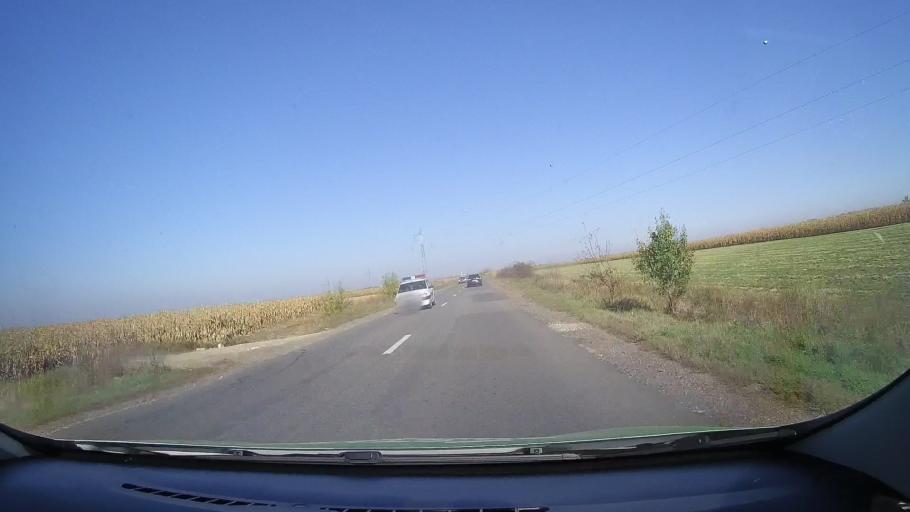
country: RO
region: Satu Mare
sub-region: Comuna Cauas
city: Cauas
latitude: 47.6068
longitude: 22.5416
